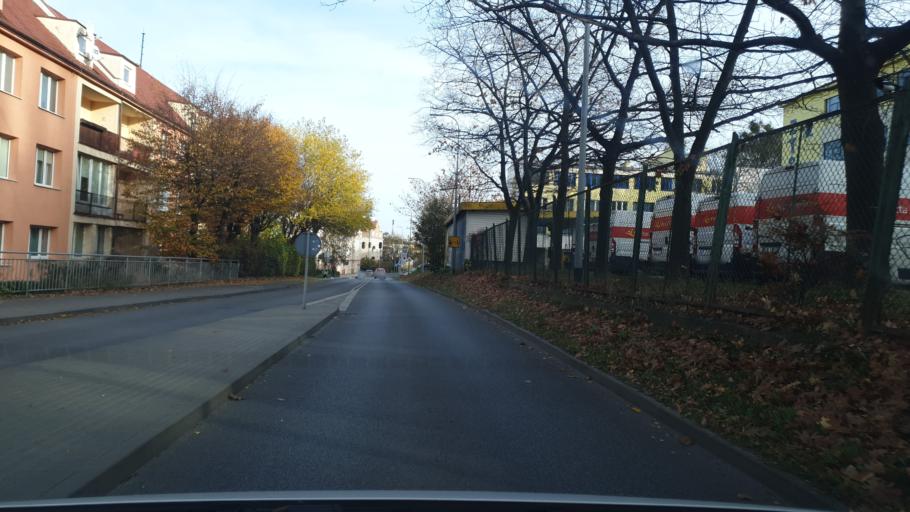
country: PL
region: Pomeranian Voivodeship
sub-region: Gdansk
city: Gdansk
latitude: 54.3793
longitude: 18.5915
